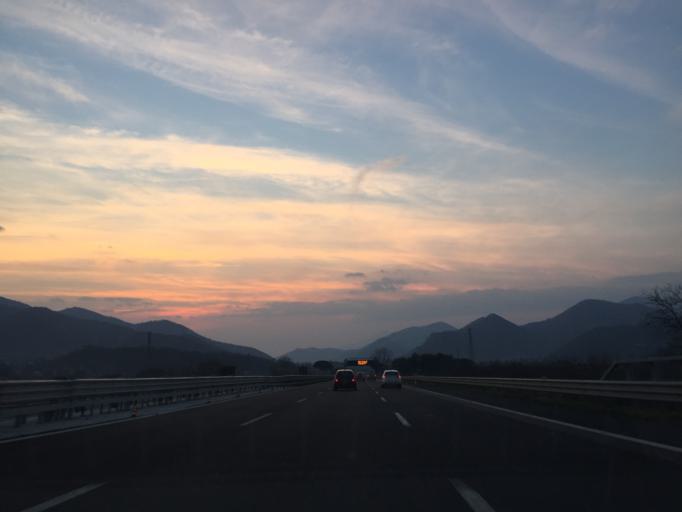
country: IT
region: Campania
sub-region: Provincia di Salerno
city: Lancusi-Penta-Bolano
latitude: 40.7724
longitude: 14.7766
